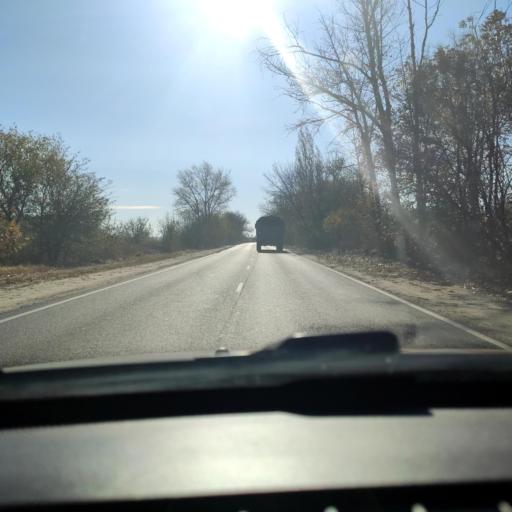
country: RU
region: Voronezj
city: Shilovo
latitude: 51.5679
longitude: 39.1394
